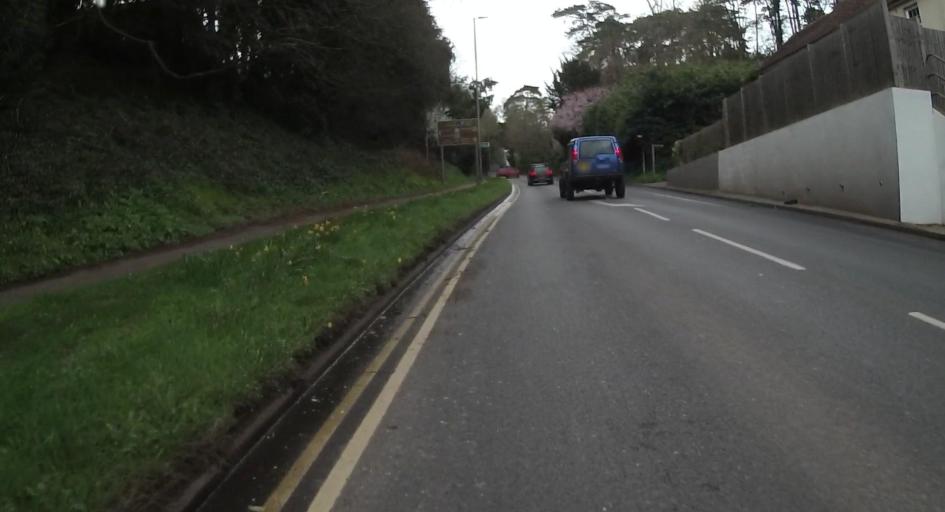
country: GB
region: England
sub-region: Surrey
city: Farnham
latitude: 51.1994
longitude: -0.7918
